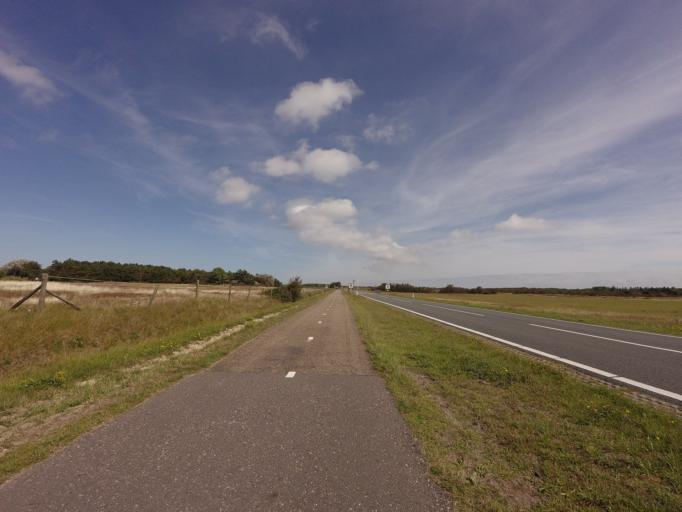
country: NL
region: Friesland
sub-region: Gemeente Ameland
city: Hollum
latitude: 53.4456
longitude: 5.6593
